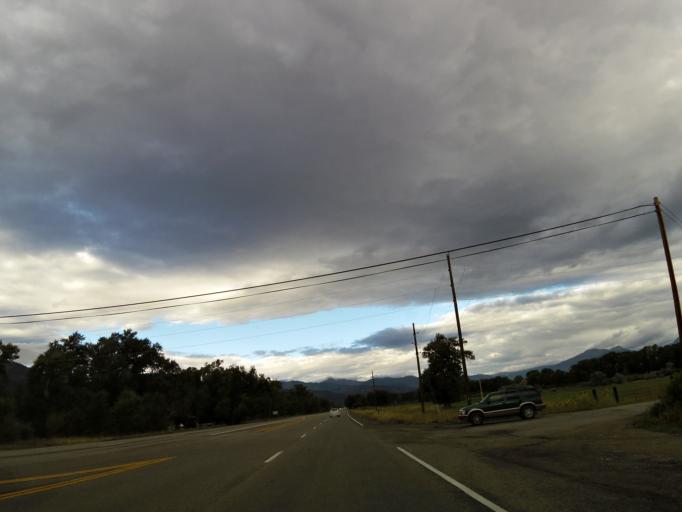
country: US
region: Colorado
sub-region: Chaffee County
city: Salida
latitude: 38.5215
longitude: -106.0335
